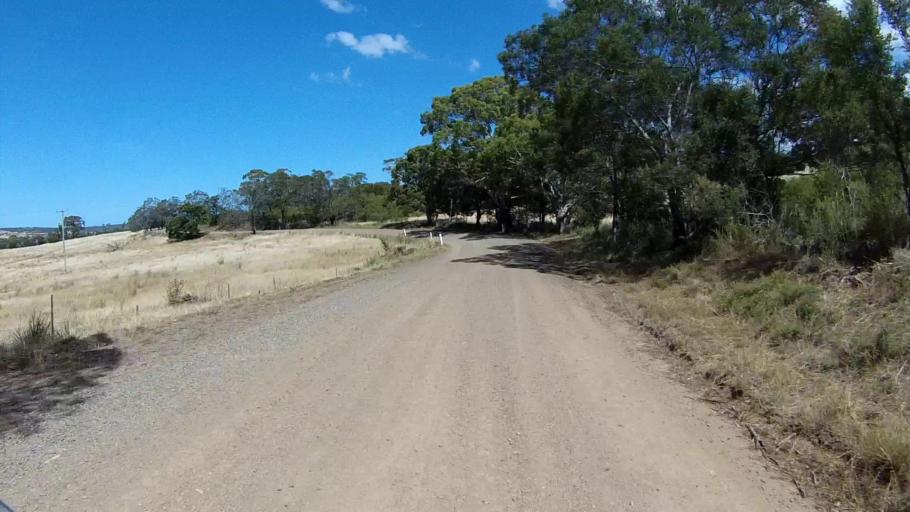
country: AU
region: Tasmania
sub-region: Break O'Day
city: St Helens
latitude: -41.9715
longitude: 148.0727
